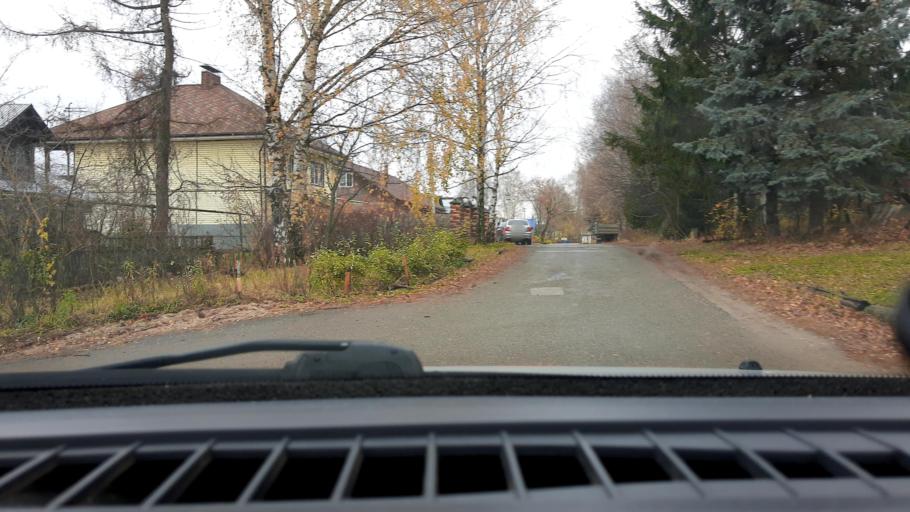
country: RU
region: Nizjnij Novgorod
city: Afonino
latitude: 56.1912
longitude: 44.0813
